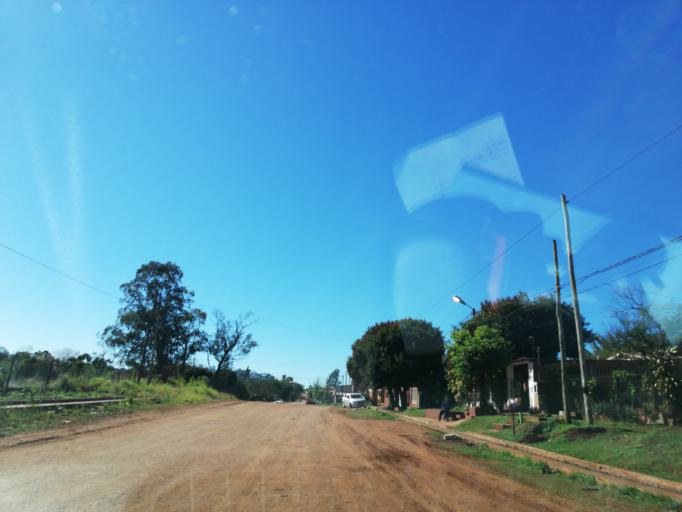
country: AR
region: Misiones
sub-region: Departamento de Capital
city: Posadas
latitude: -27.3943
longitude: -55.9329
